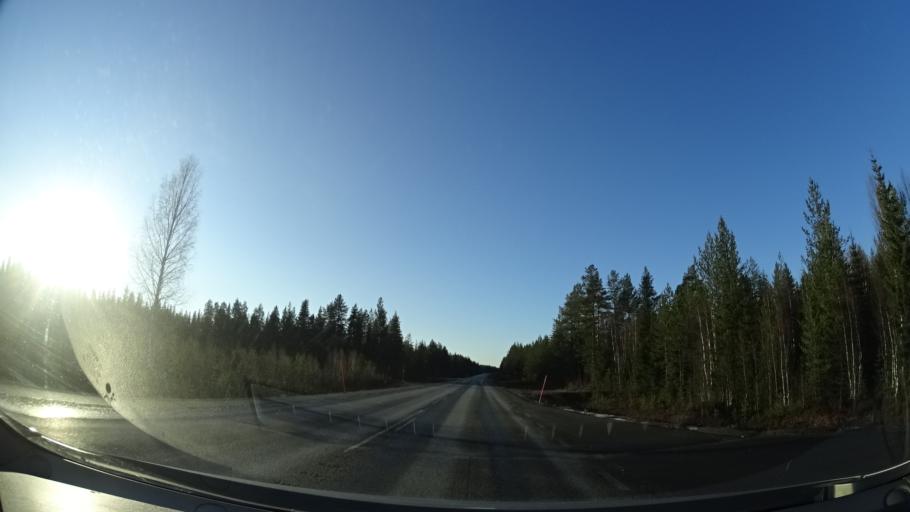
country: SE
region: Vaesterbotten
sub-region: Norsjo Kommun
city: Norsjoe
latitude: 64.9656
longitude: 19.8471
